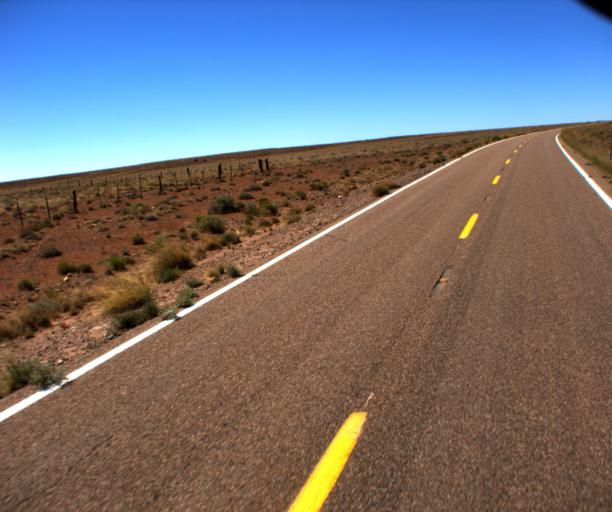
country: US
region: Arizona
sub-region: Navajo County
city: Winslow
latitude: 34.9170
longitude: -110.6378
